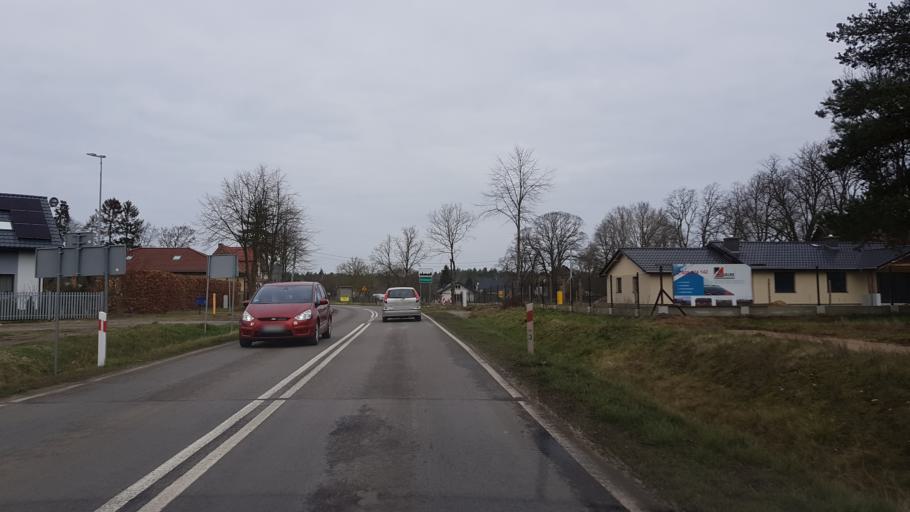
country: PL
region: West Pomeranian Voivodeship
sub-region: Powiat policki
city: Police
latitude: 53.6235
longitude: 14.5038
